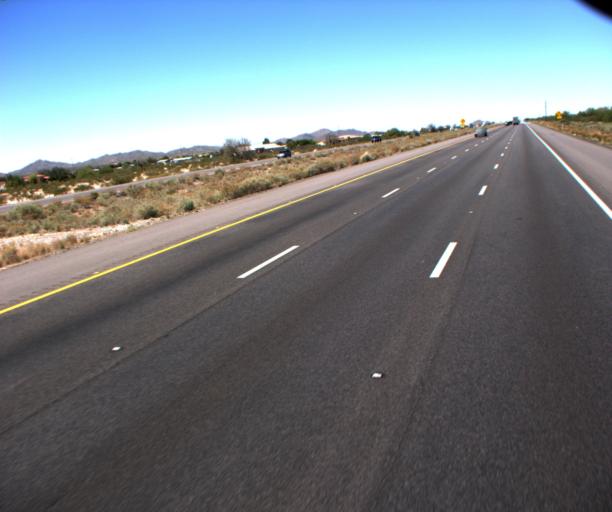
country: US
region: Arizona
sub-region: Pinal County
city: Casa Grande
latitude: 32.9752
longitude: -111.7303
